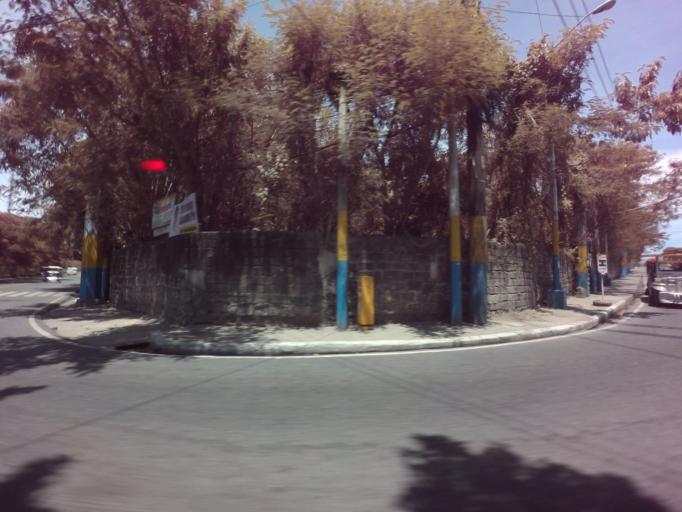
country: PH
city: Sambayanihan People's Village
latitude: 14.4525
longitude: 121.0506
